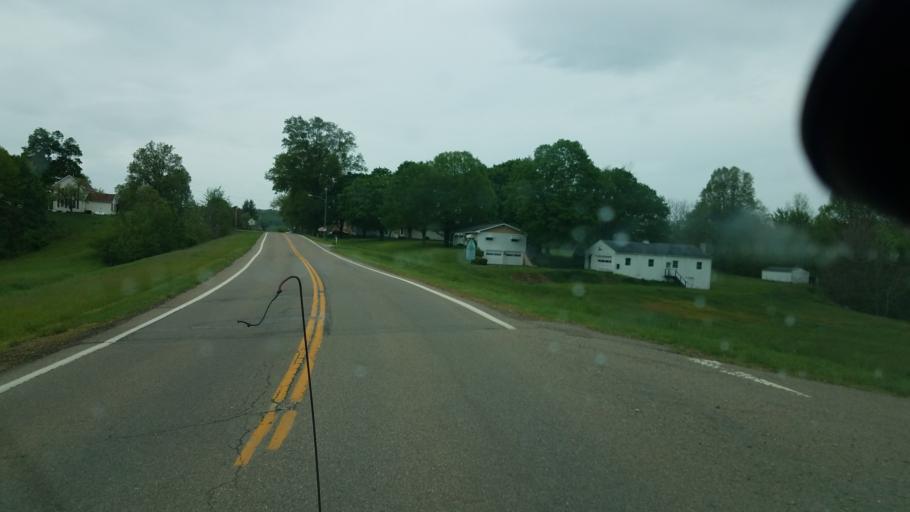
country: US
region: Ohio
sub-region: Coshocton County
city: West Lafayette
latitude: 40.2081
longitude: -81.7143
